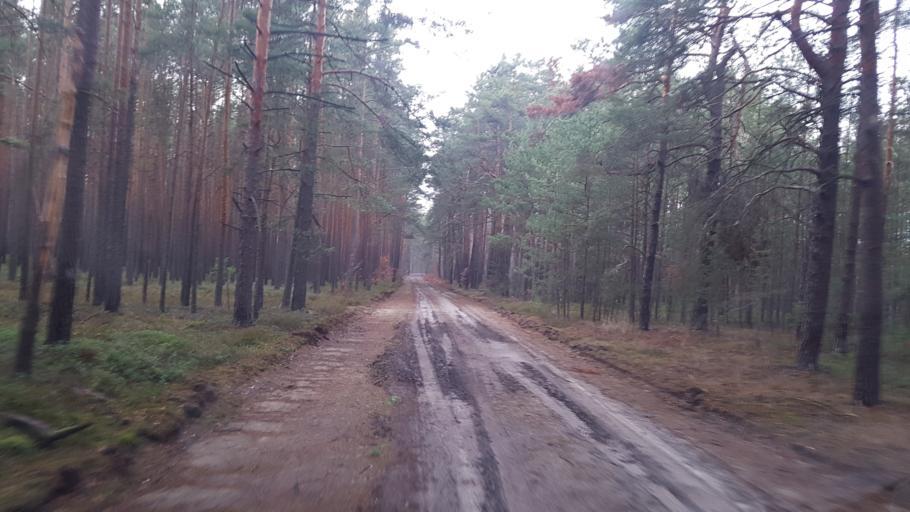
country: DE
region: Brandenburg
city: Ruckersdorf
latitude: 51.5817
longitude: 13.6083
